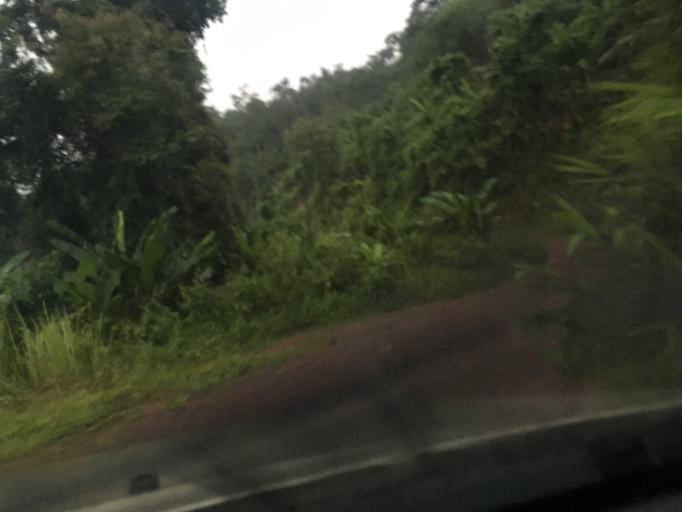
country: LA
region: Oudomxai
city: Muang La
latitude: 21.2452
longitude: 101.9397
